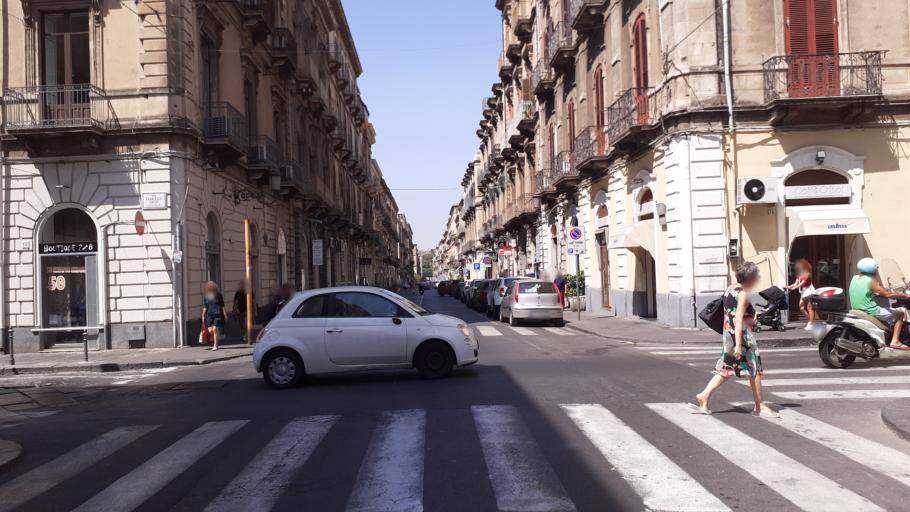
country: IT
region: Sicily
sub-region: Catania
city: Canalicchio
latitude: 37.5123
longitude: 15.0942
